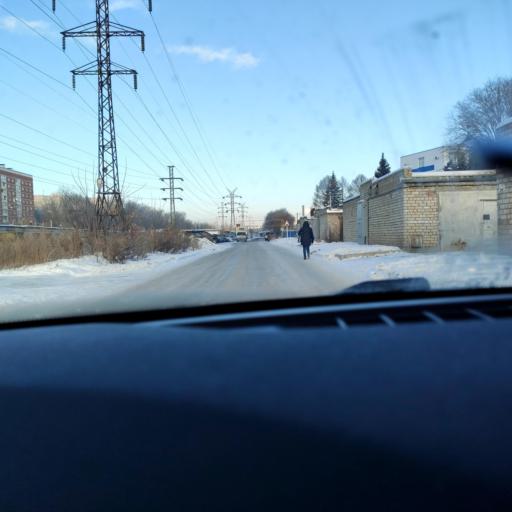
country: RU
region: Samara
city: Smyshlyayevka
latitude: 53.2082
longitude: 50.2870
